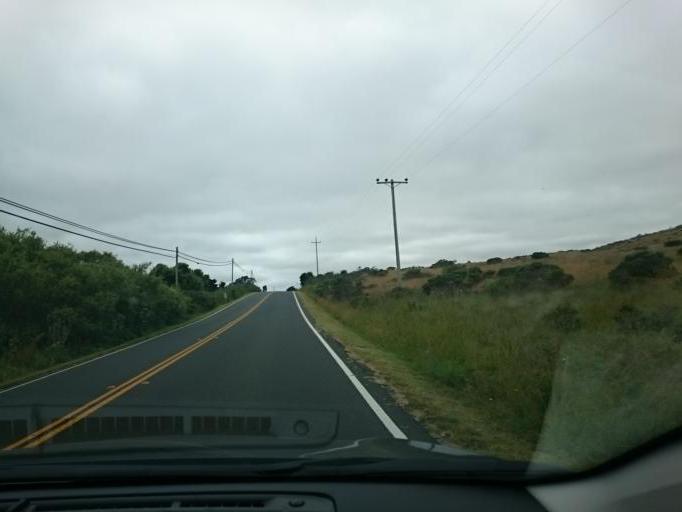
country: US
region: California
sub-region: Marin County
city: Inverness
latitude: 38.1118
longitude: -122.8485
